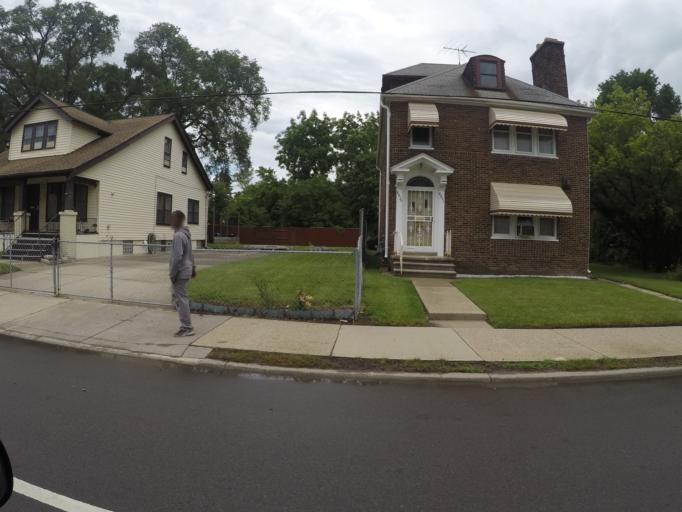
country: US
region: Michigan
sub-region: Wayne County
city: Hamtramck
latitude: 42.3794
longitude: -83.0041
